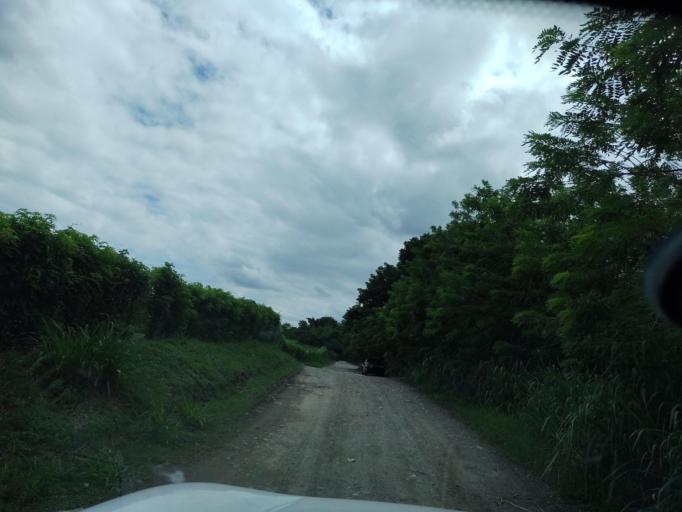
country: MX
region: Veracruz
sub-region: Martinez de la Torre
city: El Progreso
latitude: 20.1115
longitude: -97.0211
